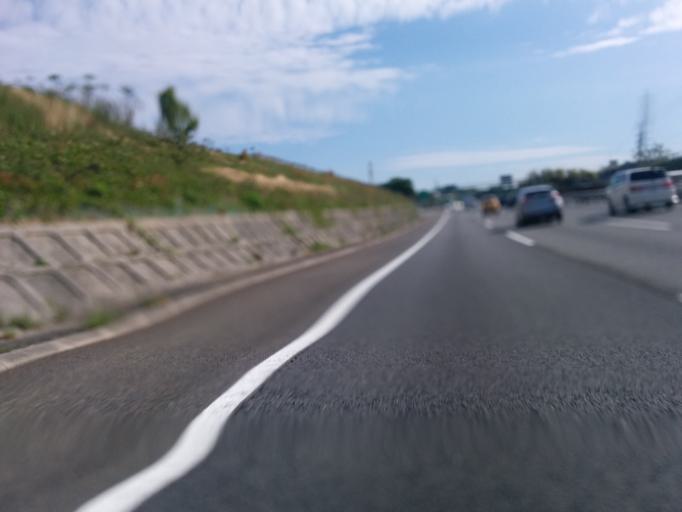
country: JP
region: Mie
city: Yokkaichi
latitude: 35.0144
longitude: 136.5883
